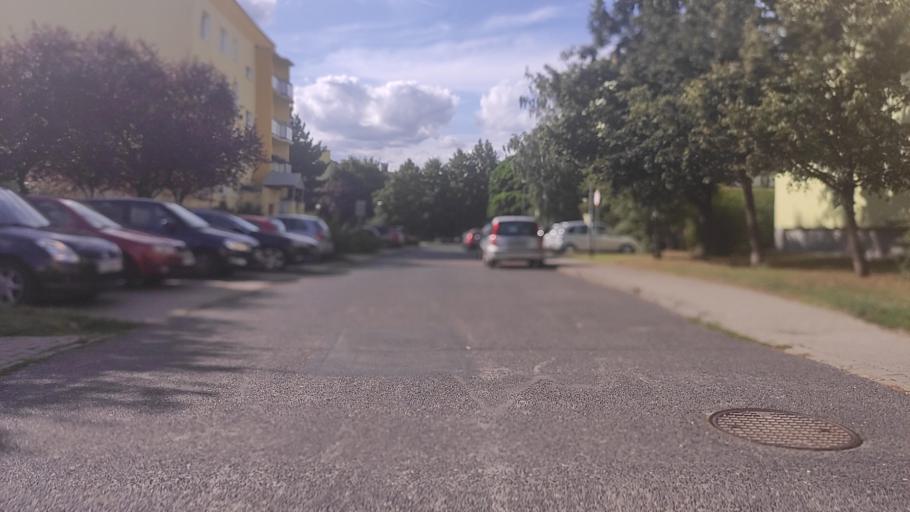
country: PL
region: Greater Poland Voivodeship
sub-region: Powiat poznanski
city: Swarzedz
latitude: 52.3991
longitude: 17.0615
